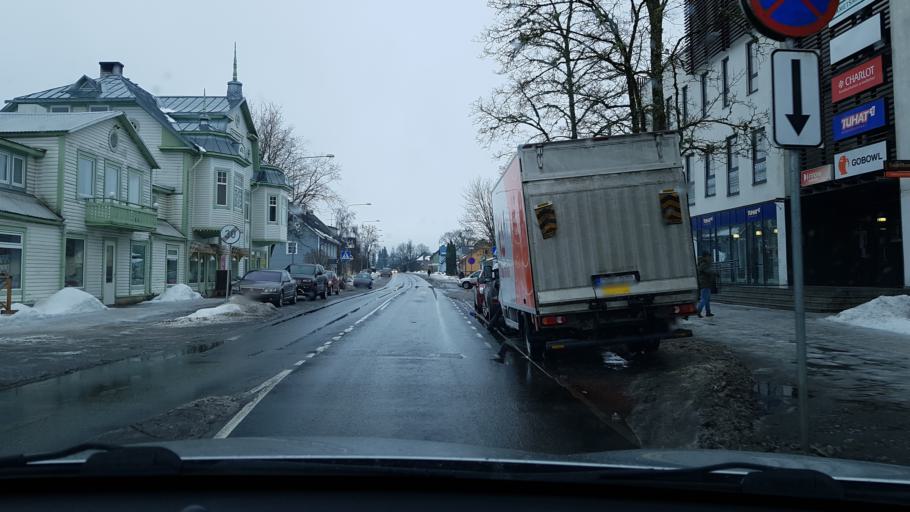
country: EE
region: Raplamaa
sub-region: Rapla vald
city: Rapla
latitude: 59.0039
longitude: 24.7933
